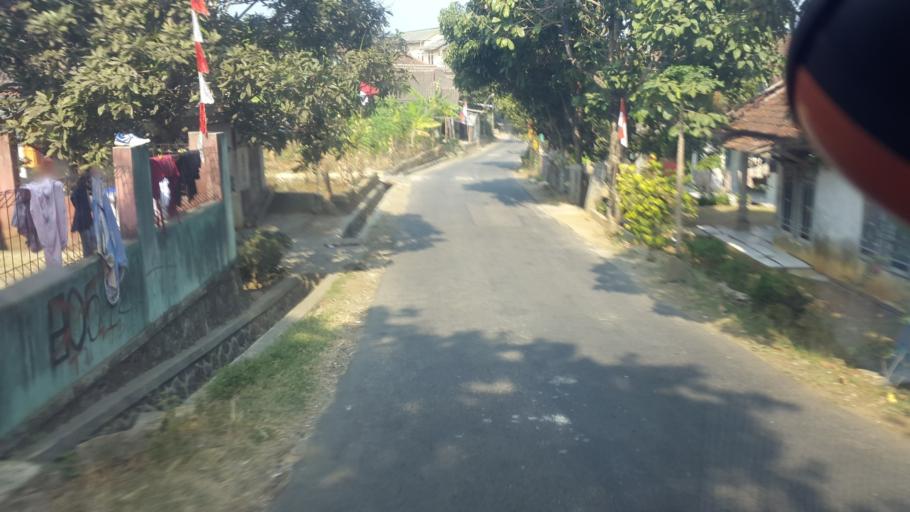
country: ID
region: West Java
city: Bojonggenteng
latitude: -7.2861
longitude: 106.6207
